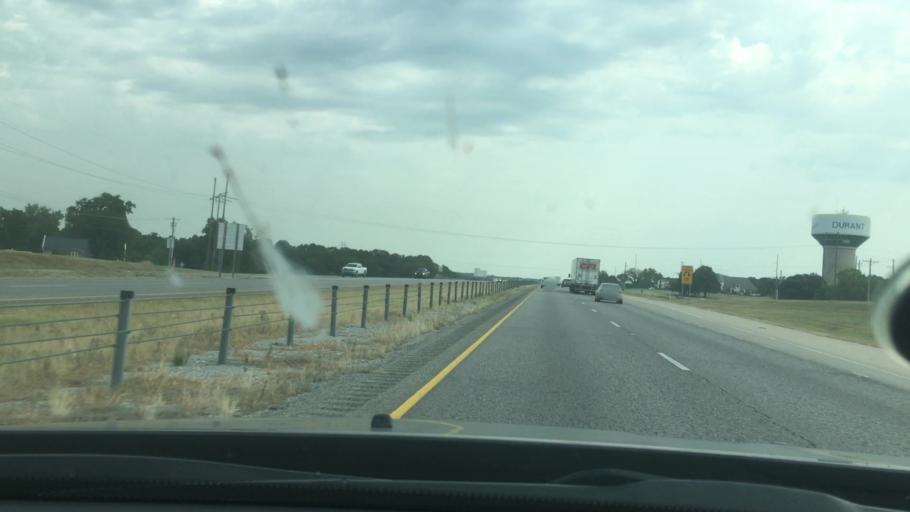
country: US
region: Oklahoma
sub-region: Bryan County
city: Durant
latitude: 34.0056
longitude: -96.3992
